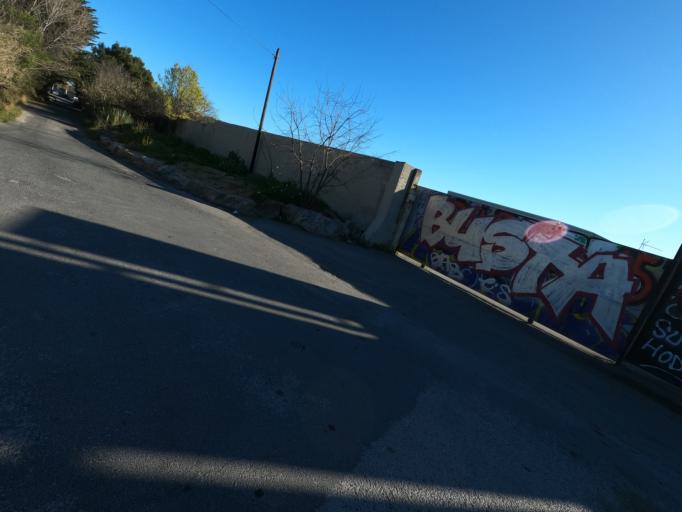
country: FR
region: Languedoc-Roussillon
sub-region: Departement de l'Herault
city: Montpellier
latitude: 43.5858
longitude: 3.8740
